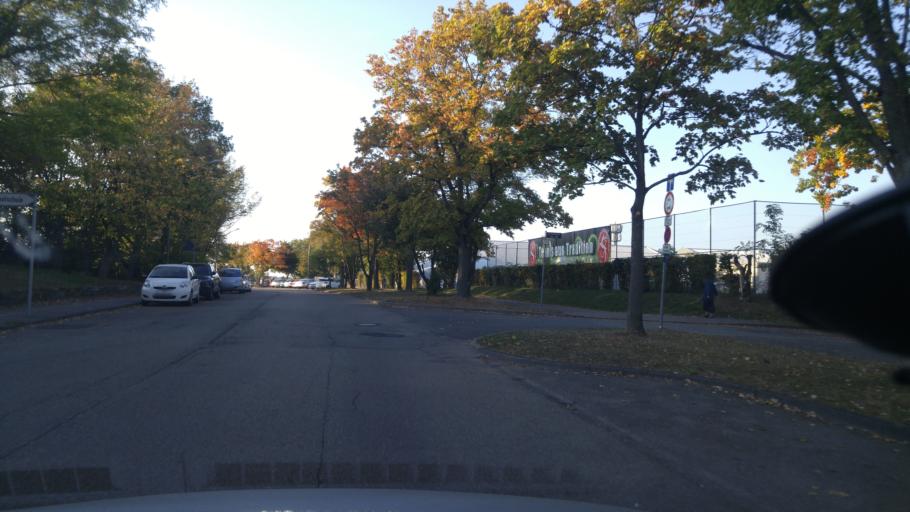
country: DE
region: Baden-Wuerttemberg
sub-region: Regierungsbezirk Stuttgart
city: Stuttgart
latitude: 48.7952
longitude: 9.1699
